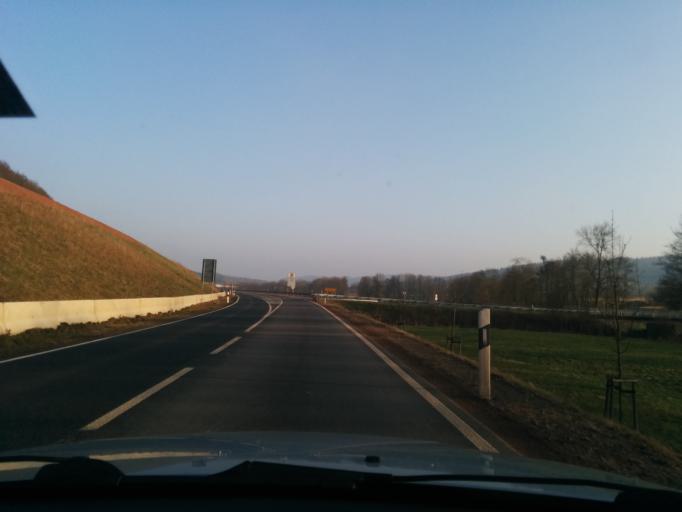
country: DE
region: Hesse
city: Waldkappel
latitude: 51.1673
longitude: 9.8337
